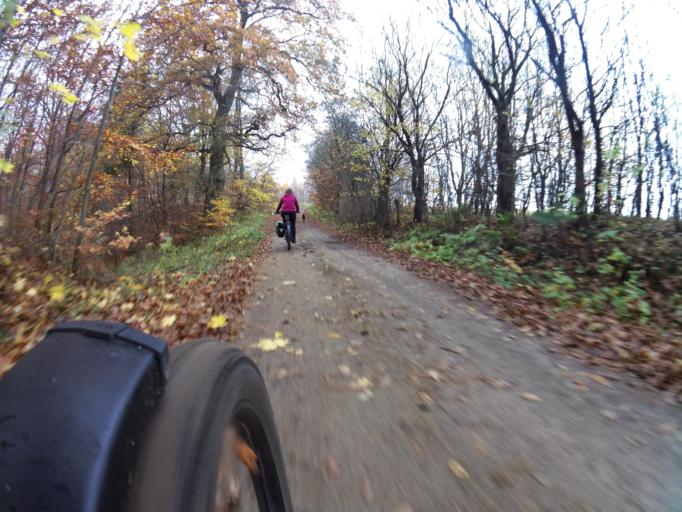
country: PL
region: Pomeranian Voivodeship
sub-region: Powiat pucki
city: Krokowa
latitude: 54.7231
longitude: 18.1328
